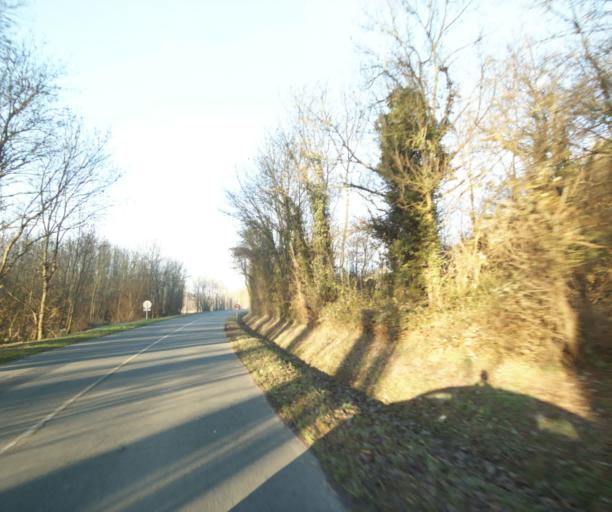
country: FR
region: Poitou-Charentes
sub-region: Departement de la Charente-Maritime
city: Cherac
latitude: 45.6864
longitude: -0.4293
